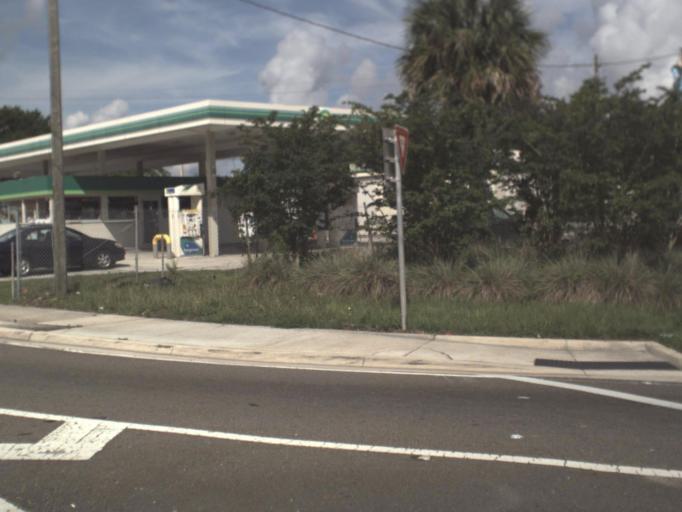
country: US
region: Florida
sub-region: Duval County
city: Jacksonville
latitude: 30.2901
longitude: -81.6307
